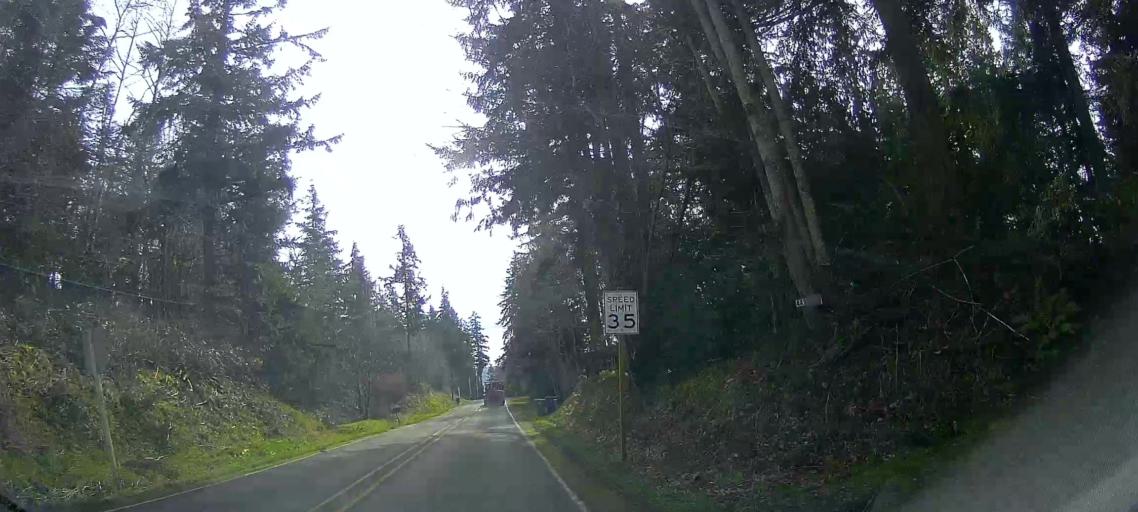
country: US
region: Washington
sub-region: Island County
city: Langley
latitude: 48.0702
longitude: -122.3877
